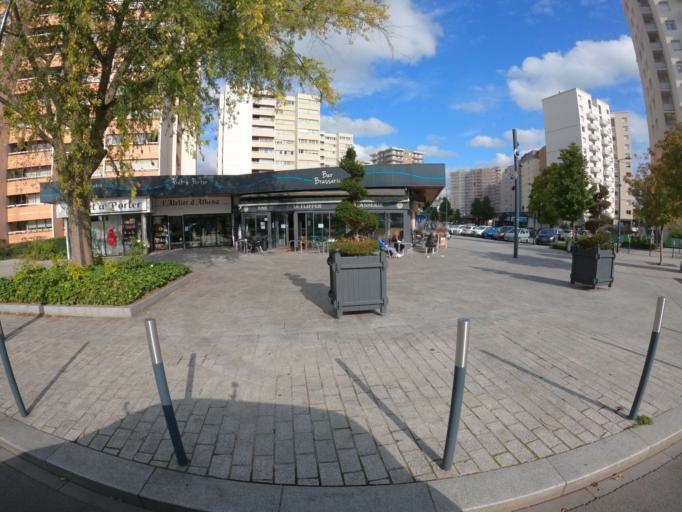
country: FR
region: Ile-de-France
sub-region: Departement de Seine-et-Marne
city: Chelles
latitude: 48.8781
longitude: 2.5912
